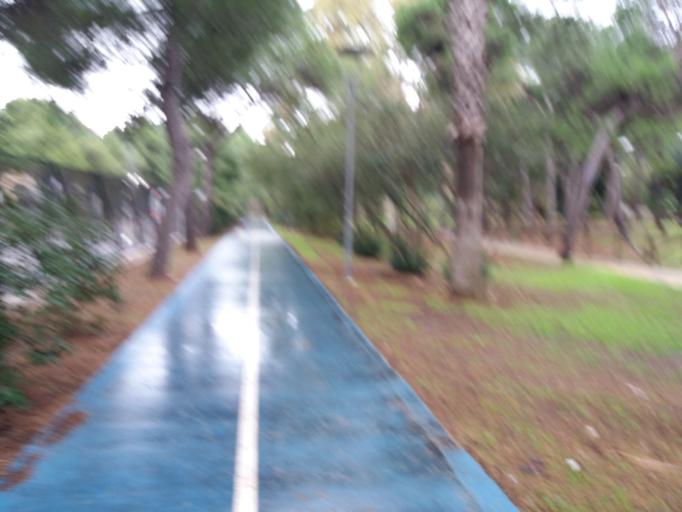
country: IT
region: Apulia
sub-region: Provincia di Bari
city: Bari
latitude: 41.1335
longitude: 16.8321
